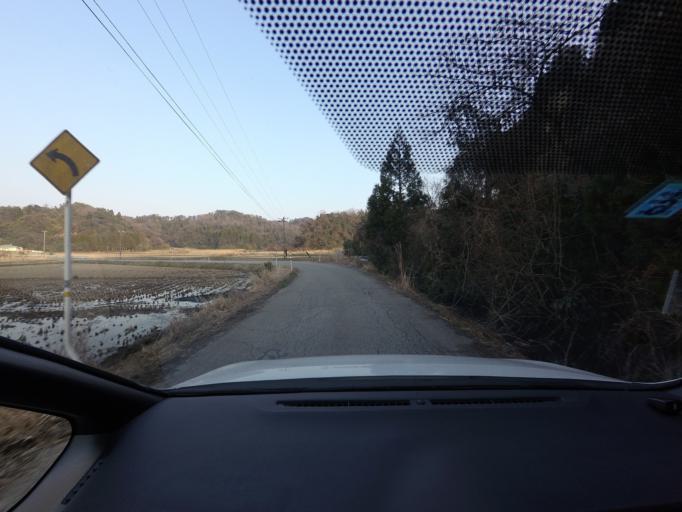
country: JP
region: Ishikawa
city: Nanao
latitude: 37.1402
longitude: 137.0124
